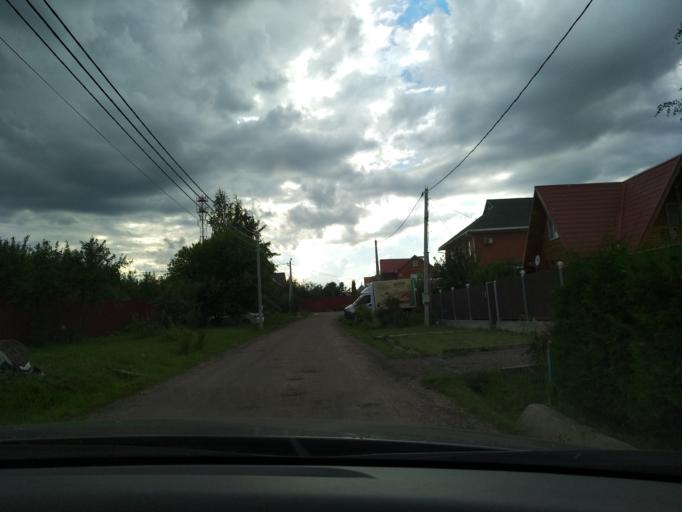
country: RU
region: Moskovskaya
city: Yegor'yevsk
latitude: 55.3663
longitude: 39.0856
